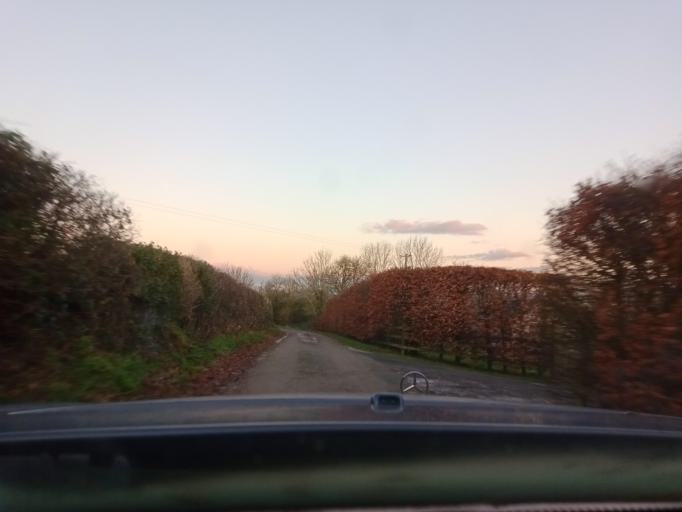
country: IE
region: Leinster
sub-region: Kilkenny
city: Graiguenamanagh
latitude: 52.5761
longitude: -6.9599
